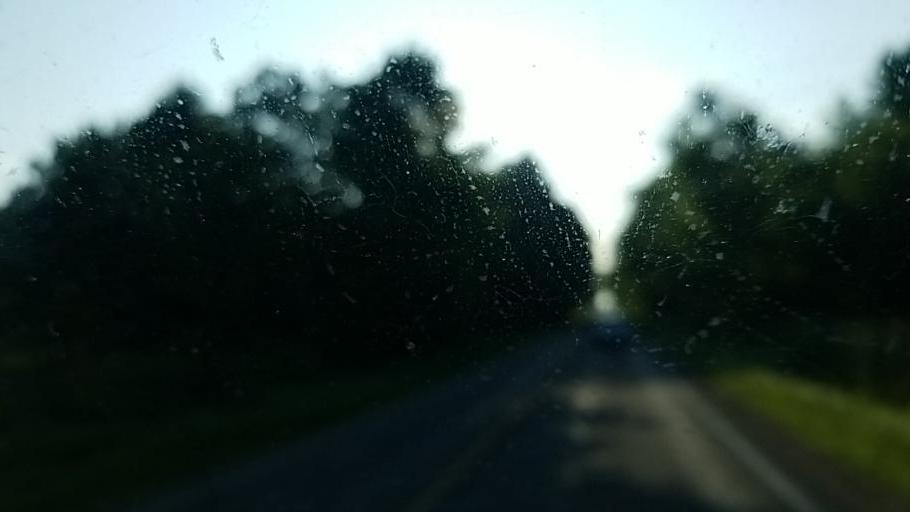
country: US
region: Michigan
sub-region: Montcalm County
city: Greenville
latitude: 43.2501
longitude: -85.2076
